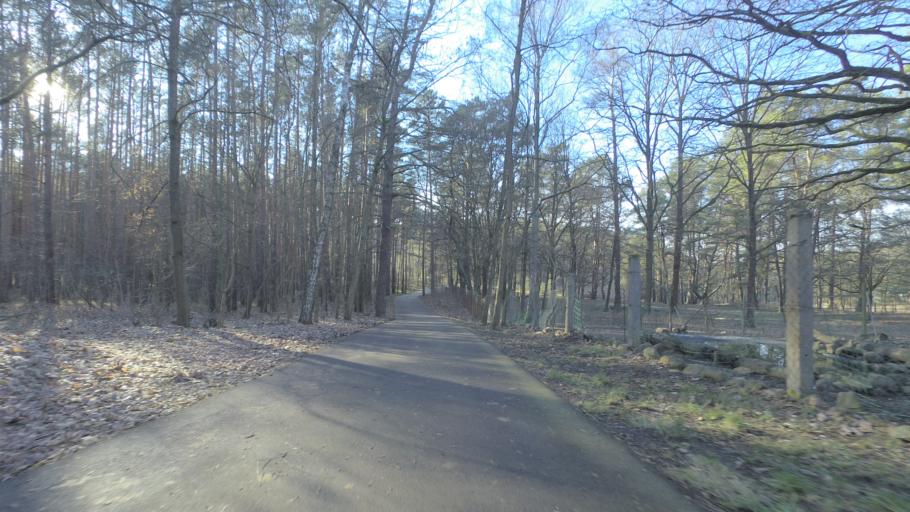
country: DE
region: Brandenburg
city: Ihlow
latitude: 52.0000
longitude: 13.3348
